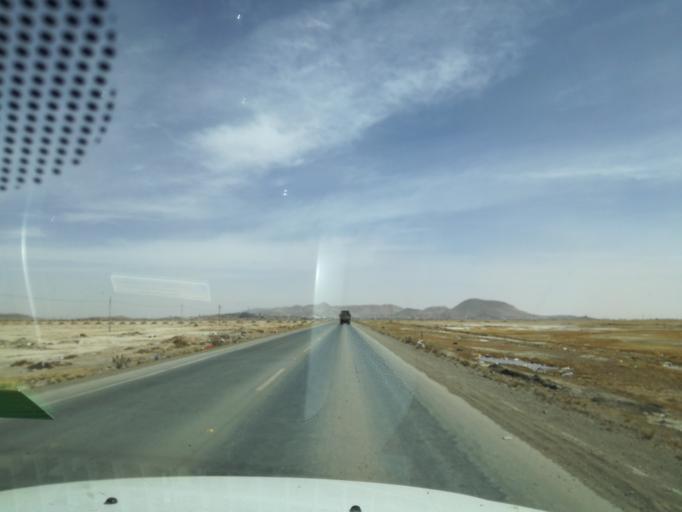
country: BO
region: Oruro
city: Oruro
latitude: -17.9008
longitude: -67.0520
